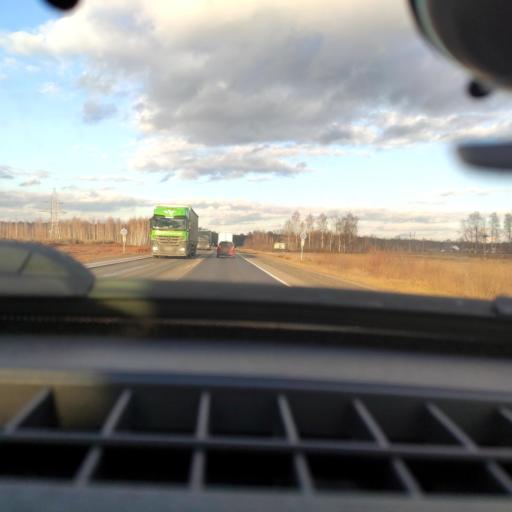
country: RU
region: Bashkortostan
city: Kabakovo
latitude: 54.7164
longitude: 56.2334
